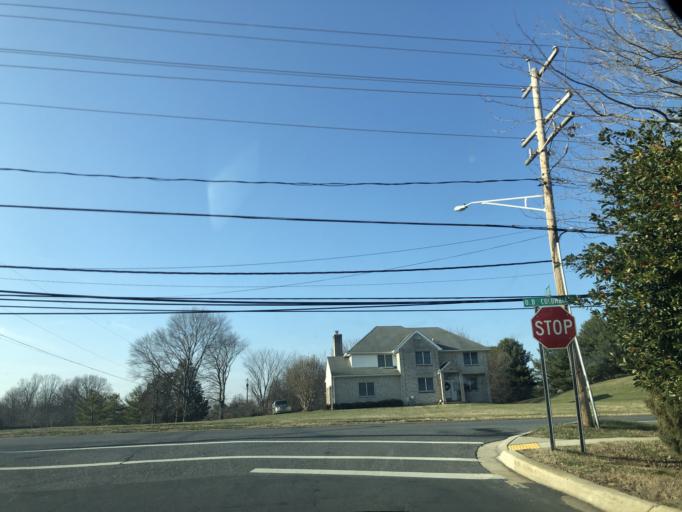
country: US
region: Maryland
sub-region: Montgomery County
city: Burtonsville
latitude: 39.1025
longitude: -76.9395
